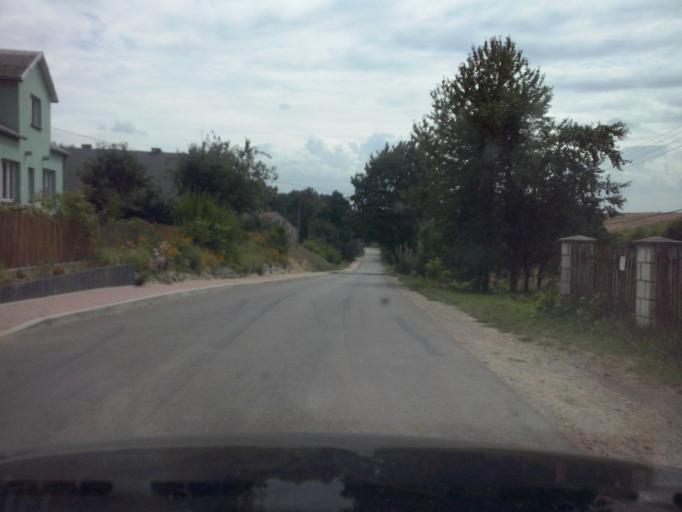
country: PL
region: Swietokrzyskie
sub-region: Powiat kielecki
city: Lagow
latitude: 50.7243
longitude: 21.1075
